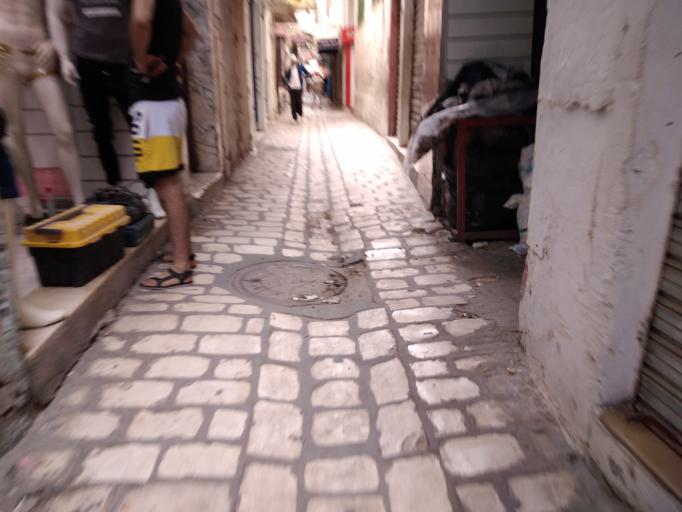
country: TN
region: Safaqis
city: Sfax
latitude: 34.7355
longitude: 10.7617
